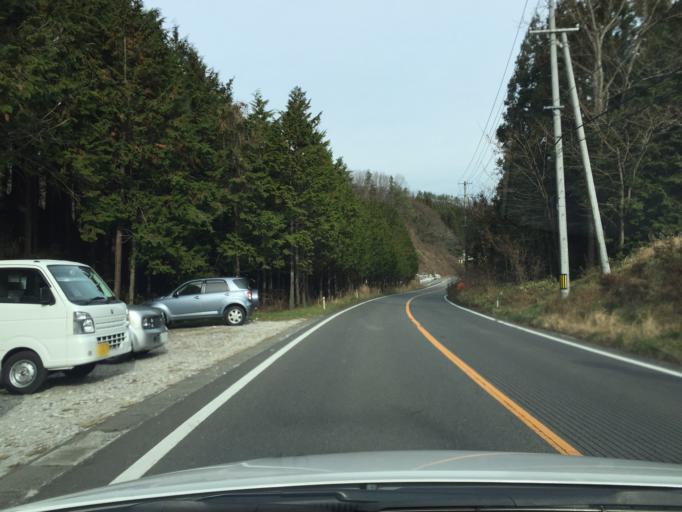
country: JP
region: Fukushima
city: Funehikimachi-funehiki
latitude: 37.2477
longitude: 140.6344
